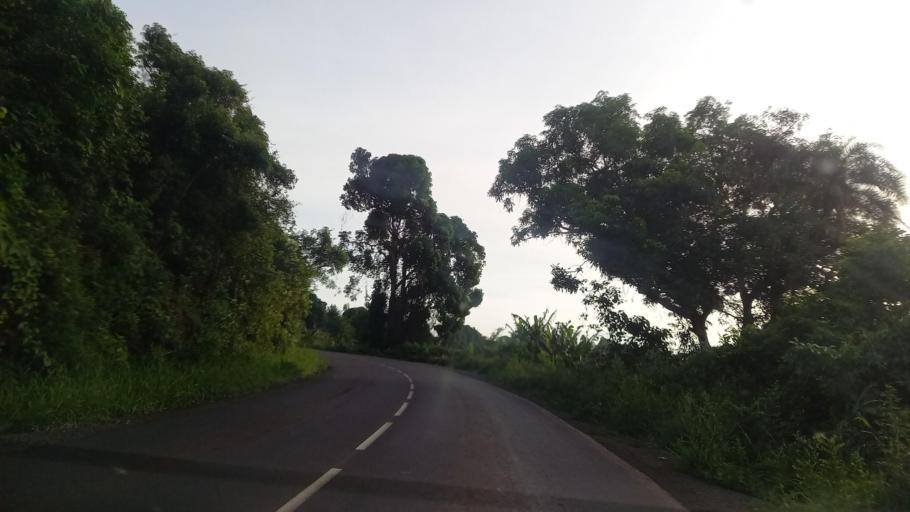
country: YT
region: Bandraboua
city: Bandraboua
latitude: -12.7374
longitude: 45.1179
